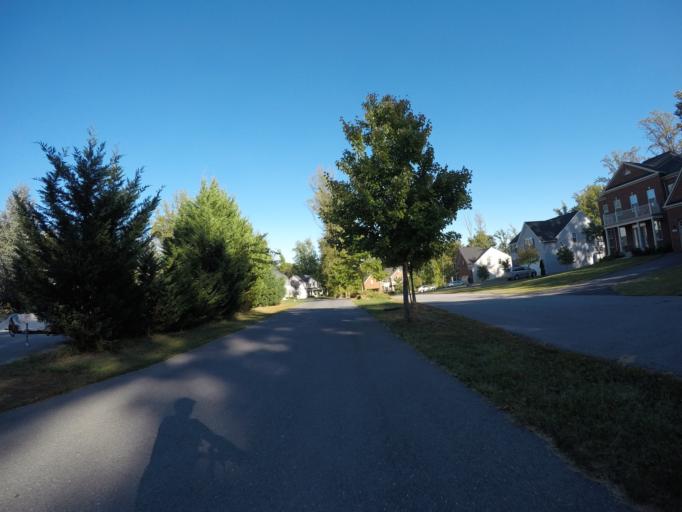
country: US
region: Maryland
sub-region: Howard County
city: Ellicott City
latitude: 39.2923
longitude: -76.8030
